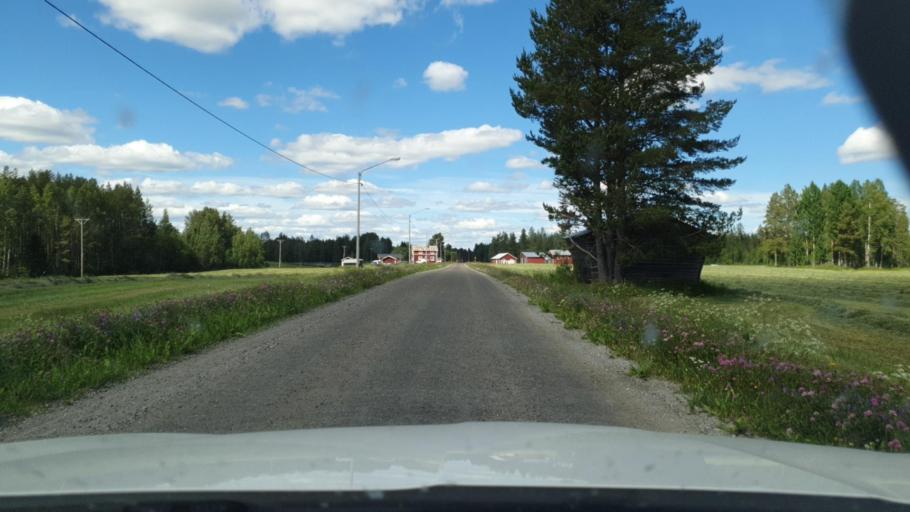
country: SE
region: Vaesterbotten
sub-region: Skelleftea Kommun
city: Backa
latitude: 65.1823
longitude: 21.0696
